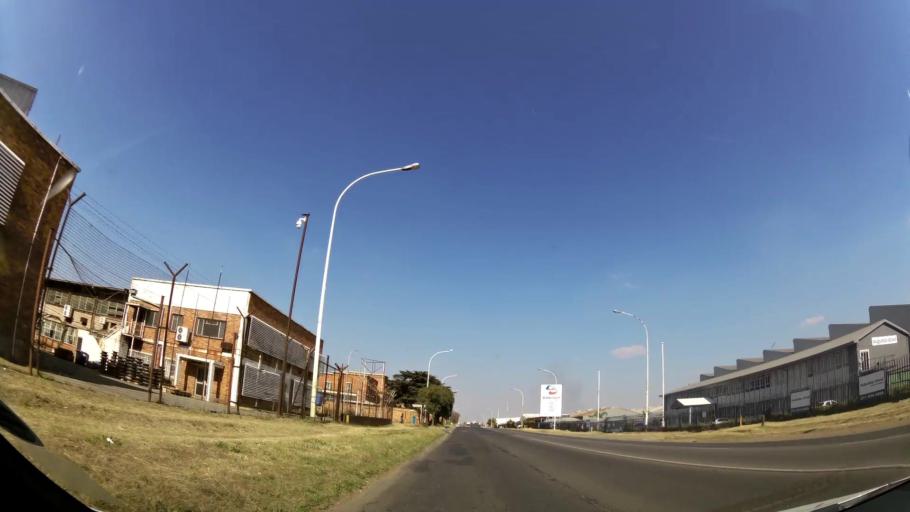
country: ZA
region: Gauteng
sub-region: Ekurhuleni Metropolitan Municipality
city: Boksburg
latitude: -26.2253
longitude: 28.2920
